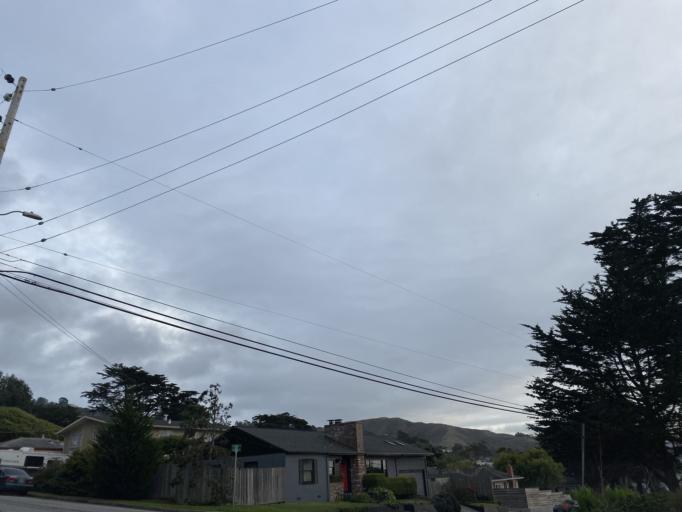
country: US
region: California
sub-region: San Mateo County
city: Broadmoor
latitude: 37.6538
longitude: -122.4867
